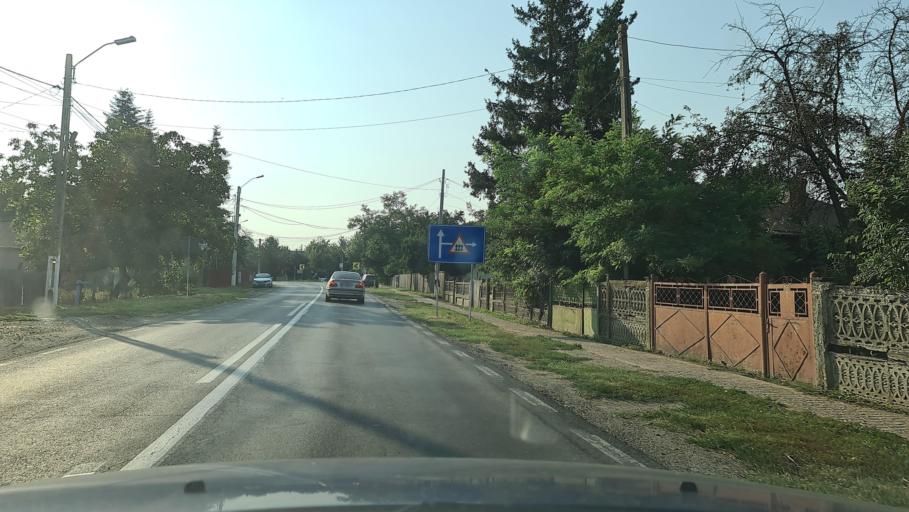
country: RO
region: Calarasi
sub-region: Comuna Dor Marunt
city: Dor Marunt
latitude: 44.4362
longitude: 26.9516
